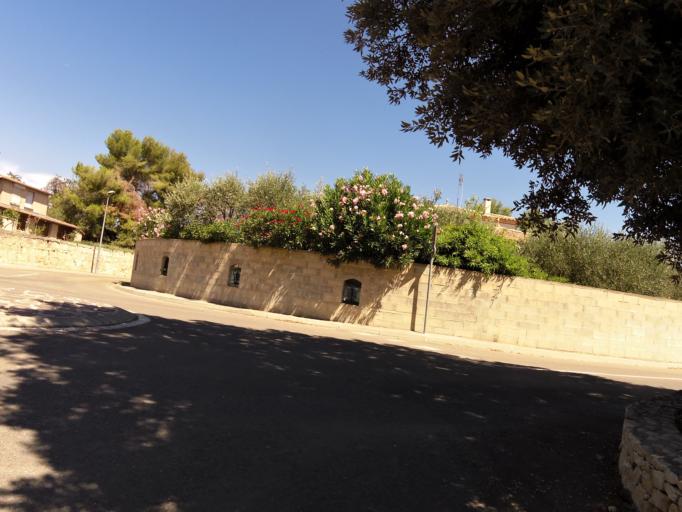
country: FR
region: Languedoc-Roussillon
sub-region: Departement du Gard
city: Vergeze
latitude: 43.7445
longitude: 4.2284
